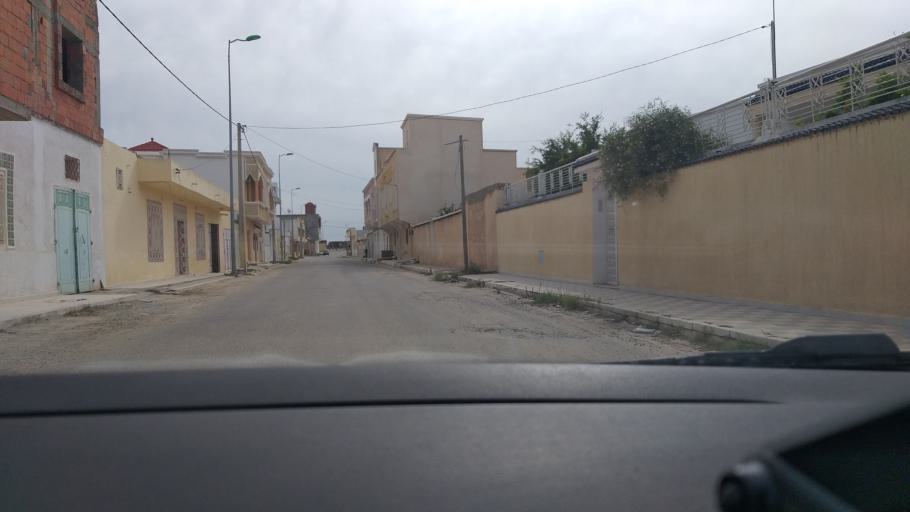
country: TN
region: Al Mahdiyah
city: El Jem
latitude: 35.2855
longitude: 10.7109
